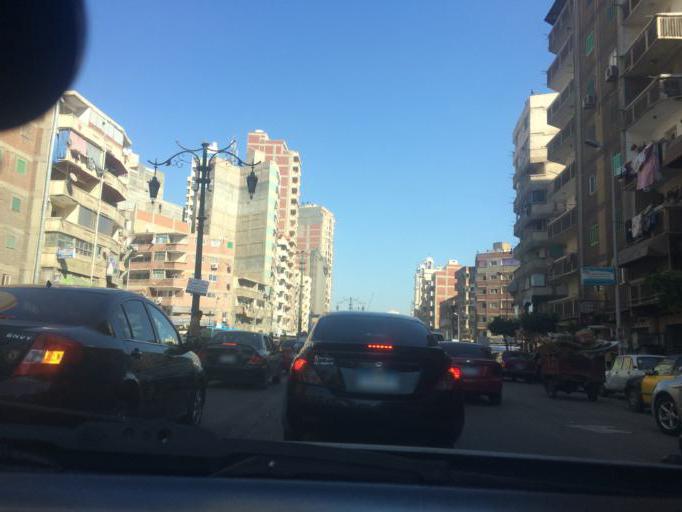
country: EG
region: Alexandria
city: Alexandria
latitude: 31.2616
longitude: 30.0096
